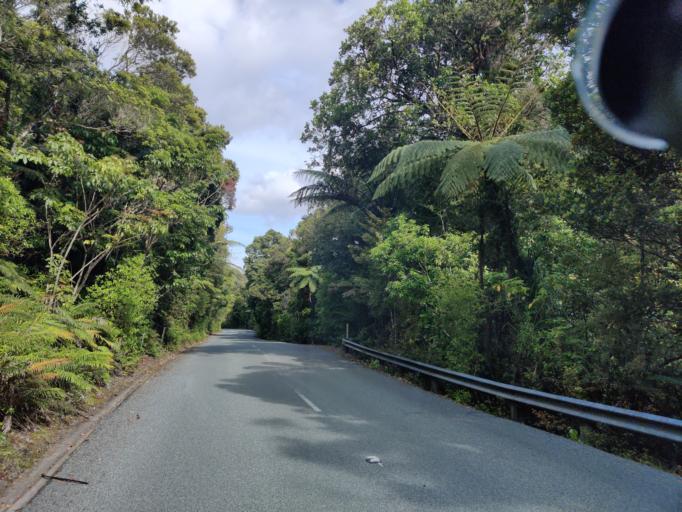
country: NZ
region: Northland
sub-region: Kaipara District
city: Dargaville
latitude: -35.6359
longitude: 173.5577
